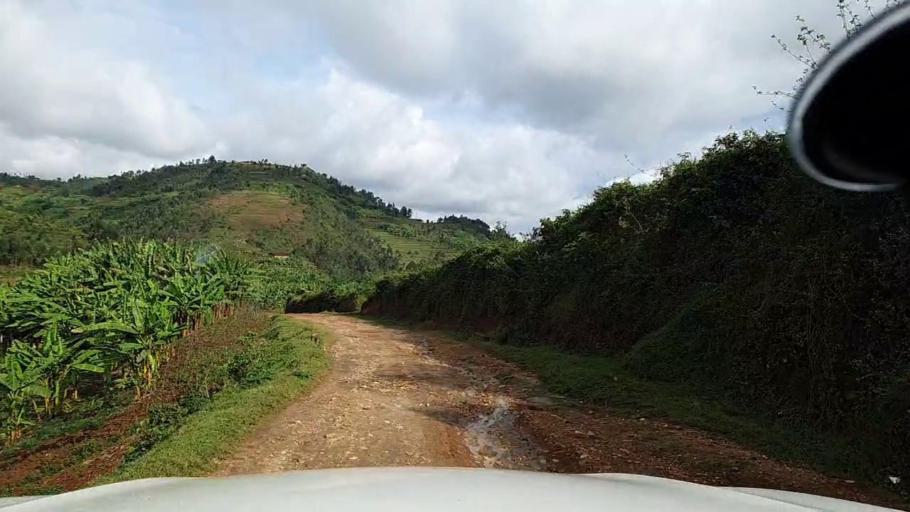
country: RW
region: Western Province
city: Kibuye
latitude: -2.1338
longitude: 29.5028
